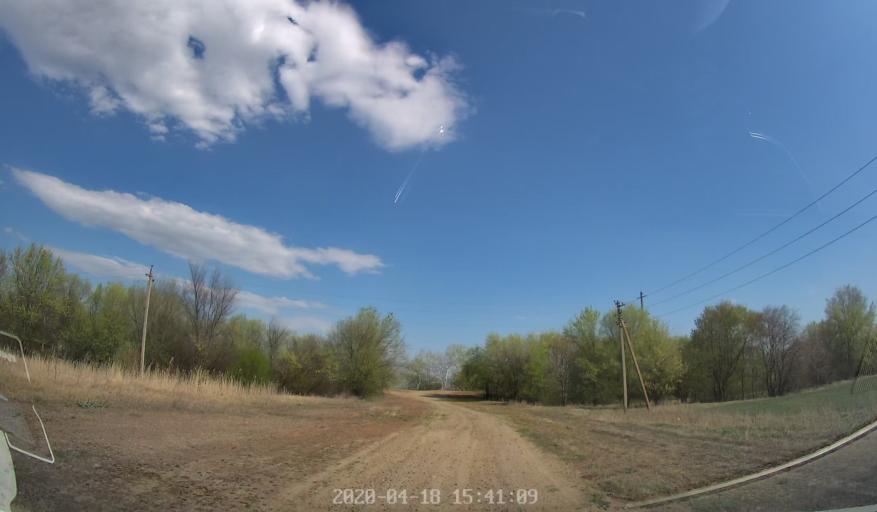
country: MD
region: Chisinau
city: Vadul lui Voda
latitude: 47.1433
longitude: 29.0951
